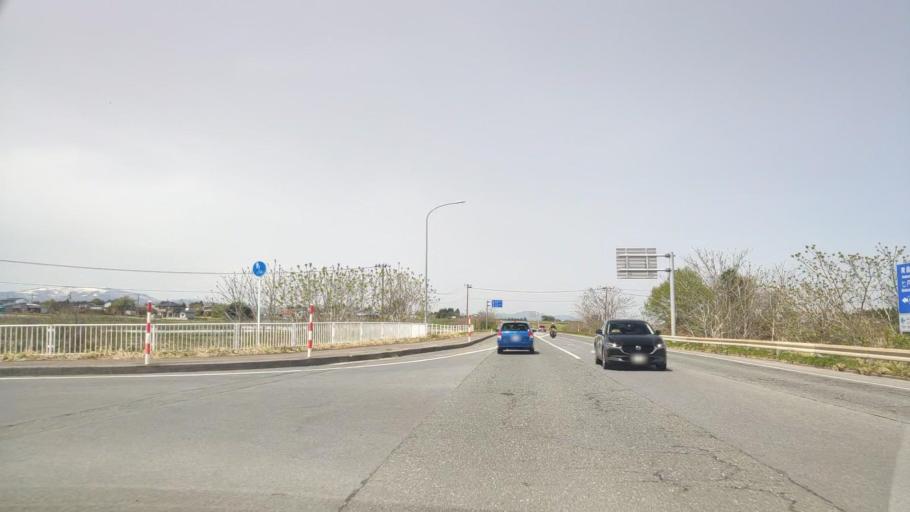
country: JP
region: Aomori
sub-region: Misawa Shi
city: Inuotose
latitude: 40.6333
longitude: 141.2458
